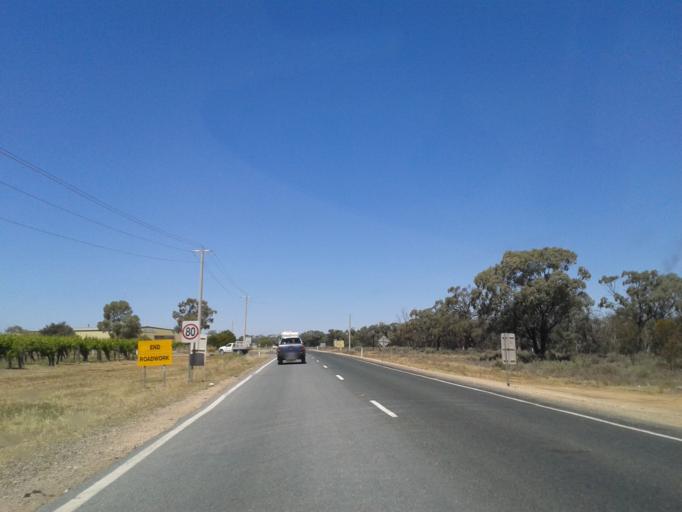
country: AU
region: New South Wales
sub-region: Wentworth
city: Gol Gol
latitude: -34.5685
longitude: 142.7301
